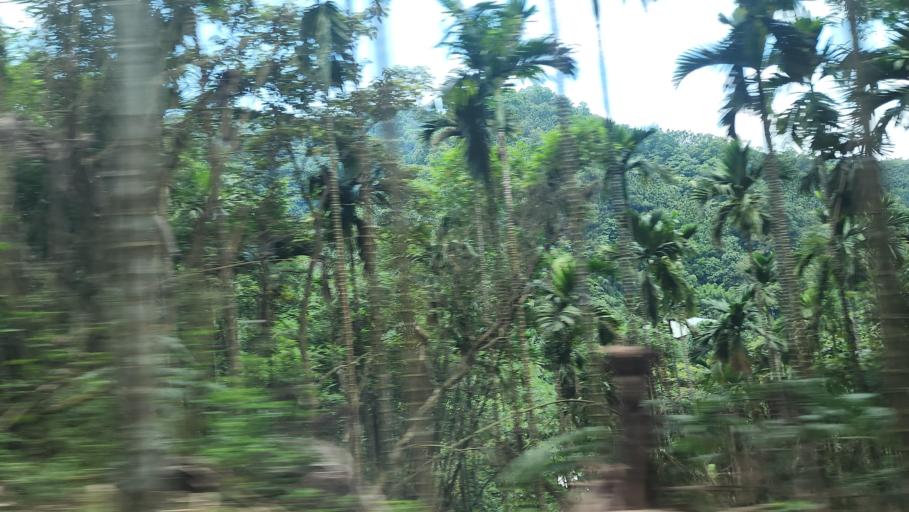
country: TW
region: Taipei
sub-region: Taipei
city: Banqiao
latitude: 24.9054
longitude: 121.4338
